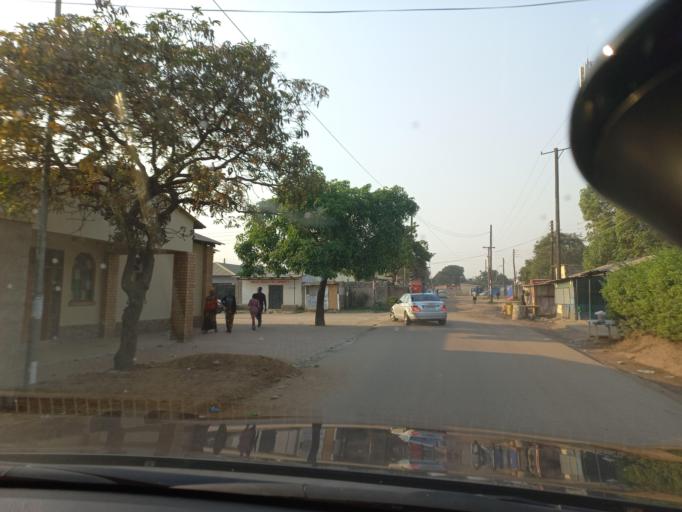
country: ZM
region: Lusaka
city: Lusaka
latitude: -15.4051
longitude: 28.3425
